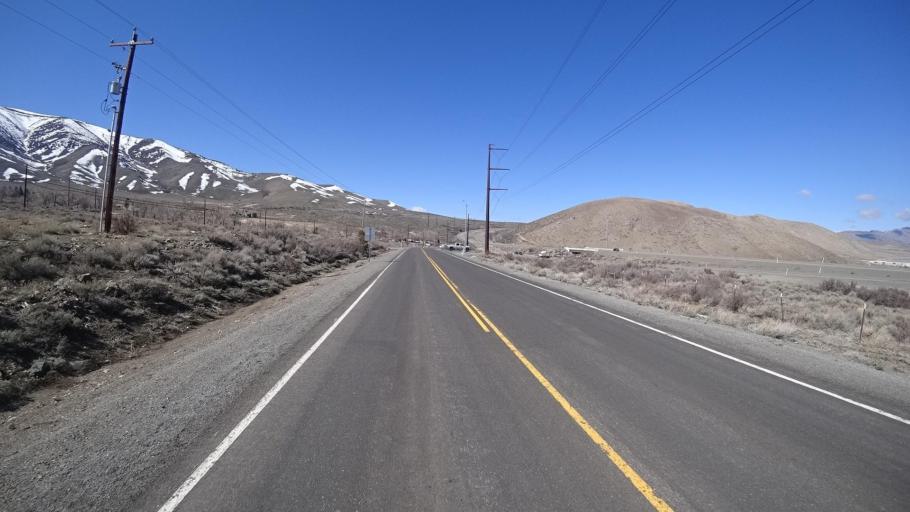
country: US
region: Nevada
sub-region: Washoe County
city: Lemmon Valley
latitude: 39.6250
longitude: -119.9139
